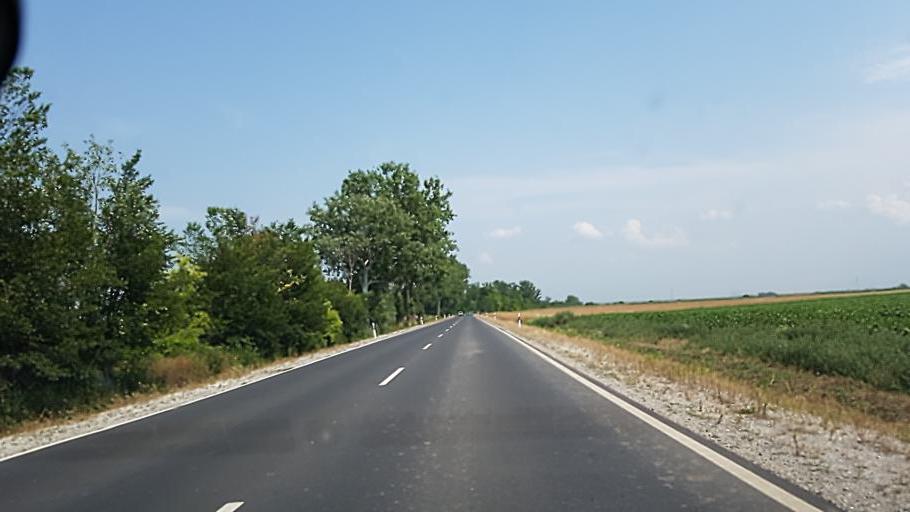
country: HU
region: Heves
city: Tiszanana
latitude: 47.6708
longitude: 20.5525
